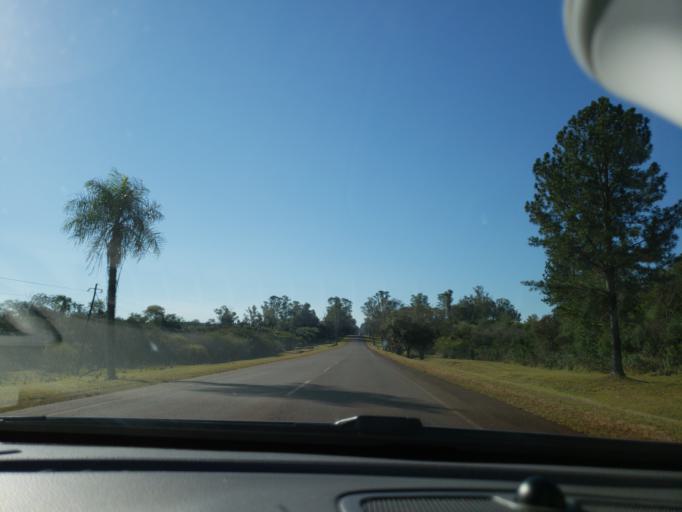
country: AR
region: Misiones
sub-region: Departamento de Apostoles
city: San Jose
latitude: -27.8216
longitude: -55.7701
